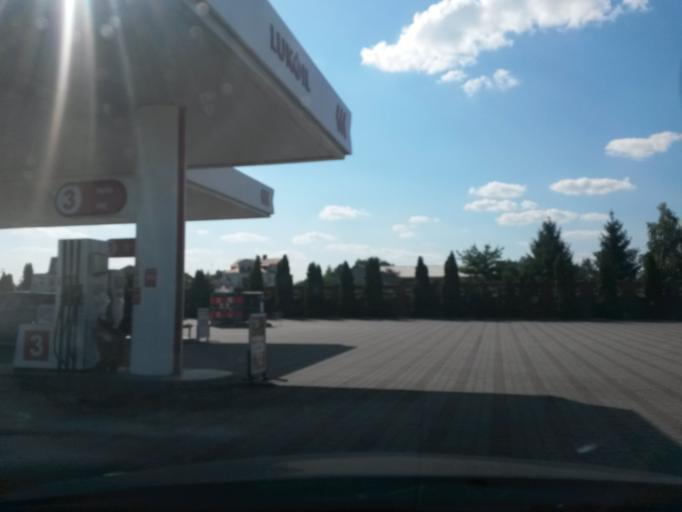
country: PL
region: Masovian Voivodeship
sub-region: Powiat plonski
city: Dzierzaznia
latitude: 52.6294
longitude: 20.2207
